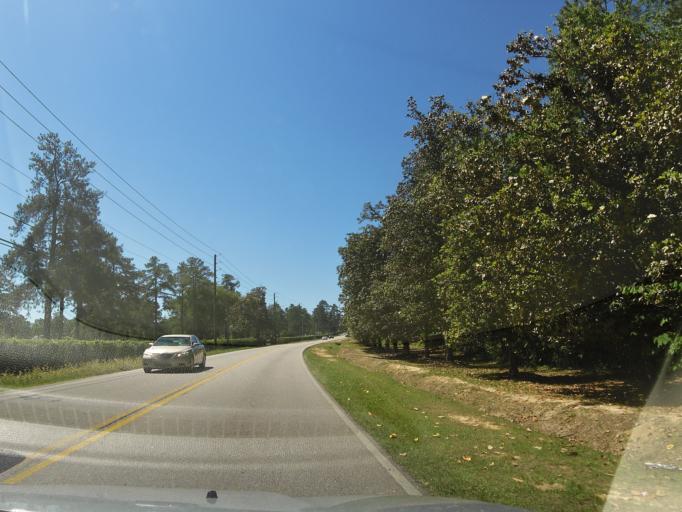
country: US
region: Georgia
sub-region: Columbia County
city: Martinez
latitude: 33.4893
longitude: -82.0292
